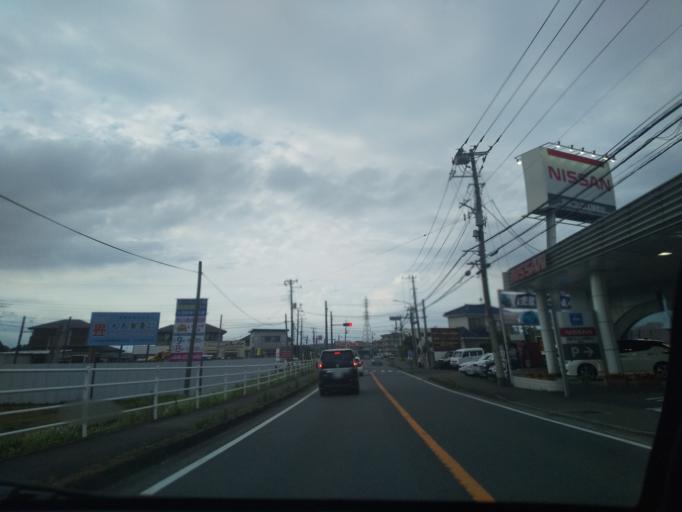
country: JP
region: Kanagawa
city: Zama
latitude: 35.4763
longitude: 139.3891
